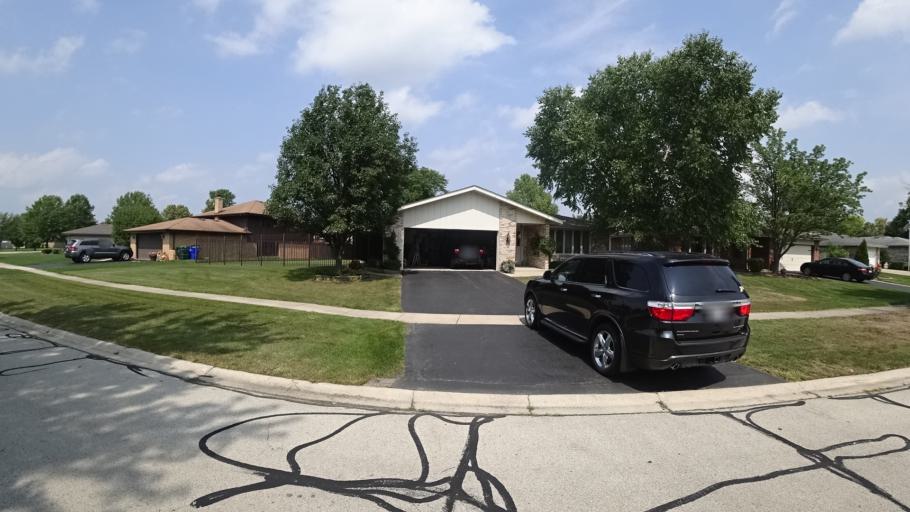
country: US
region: Illinois
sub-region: Will County
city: Goodings Grove
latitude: 41.6240
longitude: -87.9005
